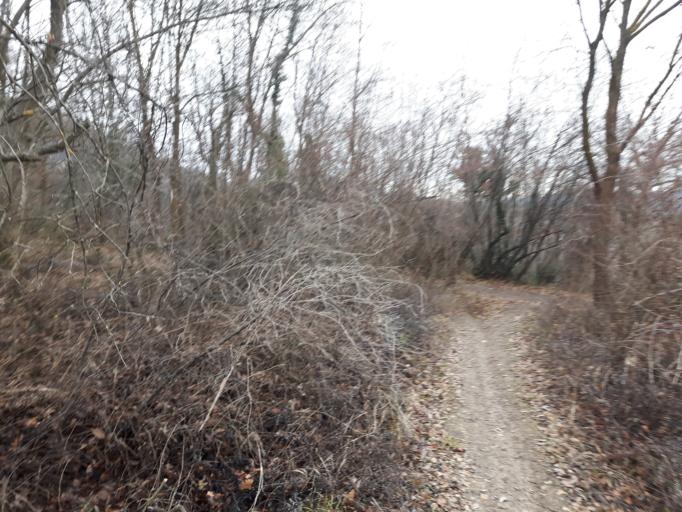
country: IT
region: Veneto
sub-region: Provincia di Padova
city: Arqua Petrarca
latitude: 45.2762
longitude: 11.7424
